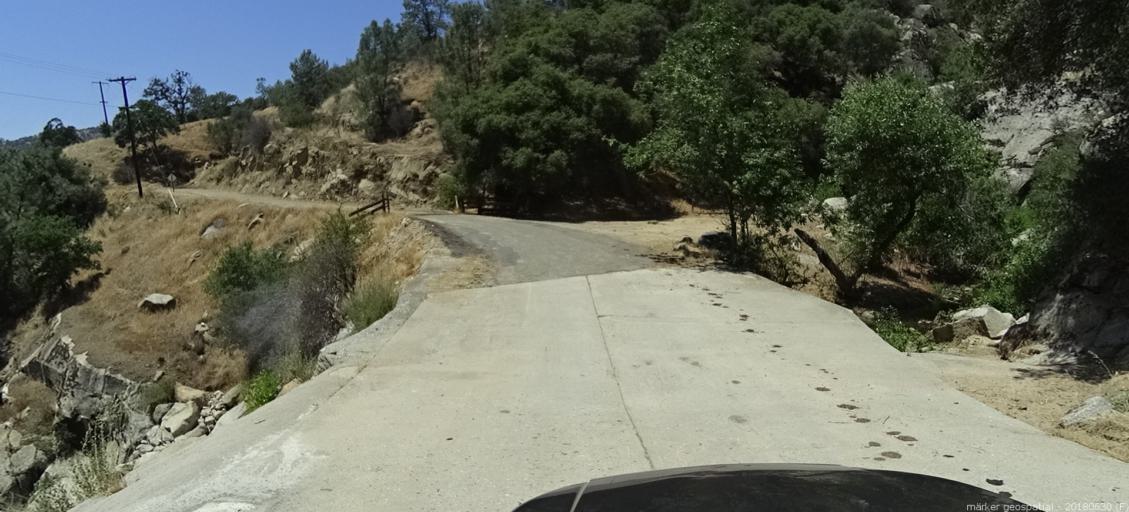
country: US
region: California
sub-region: Fresno County
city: Auberry
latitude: 37.1658
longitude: -119.4165
